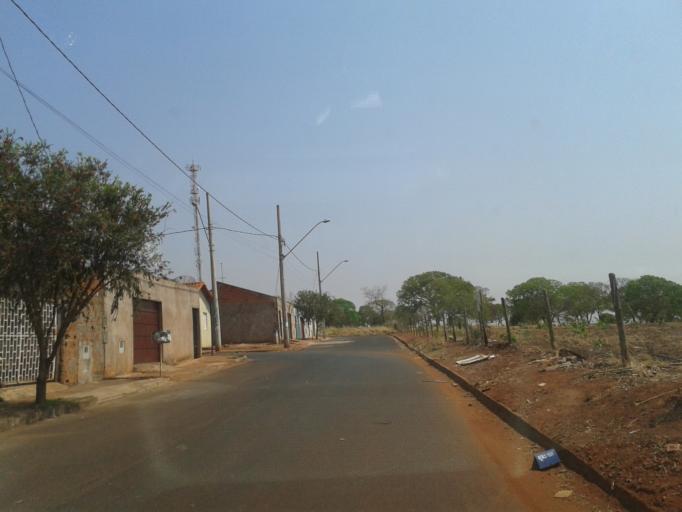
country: BR
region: Minas Gerais
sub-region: Ituiutaba
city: Ituiutaba
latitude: -18.9800
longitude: -49.4312
